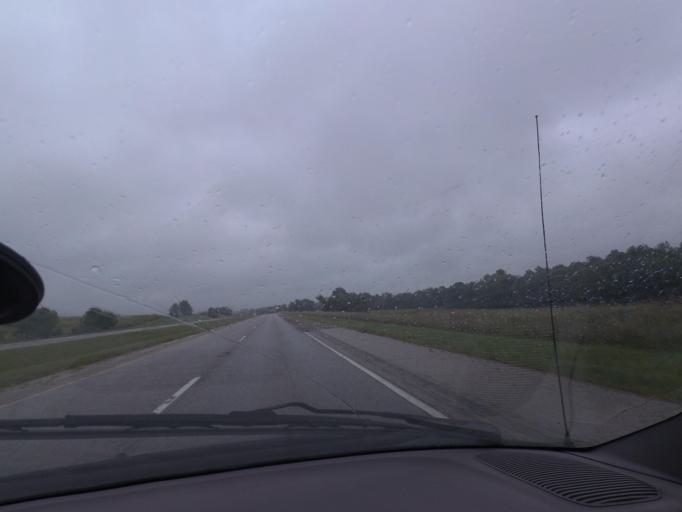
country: US
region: Illinois
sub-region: Pike County
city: Pittsfield
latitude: 39.6773
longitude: -90.8654
